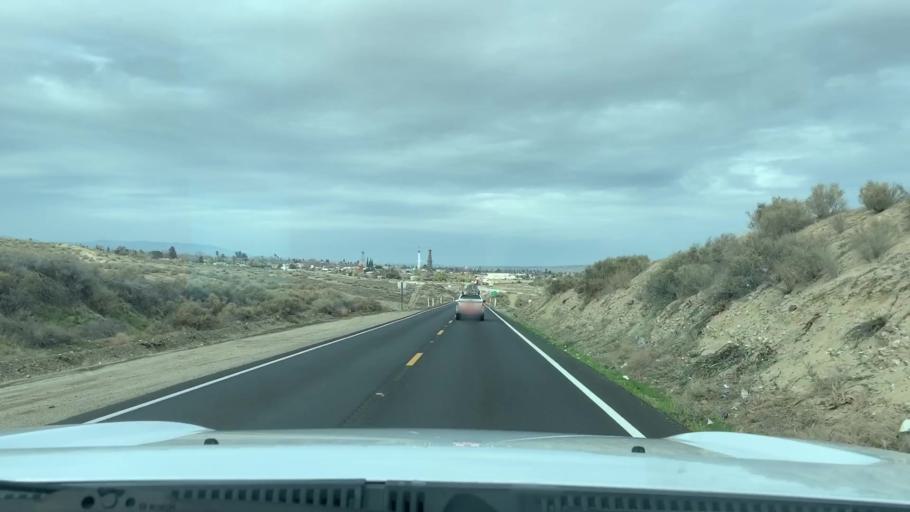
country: US
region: California
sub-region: Kern County
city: South Taft
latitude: 35.1275
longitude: -119.4415
